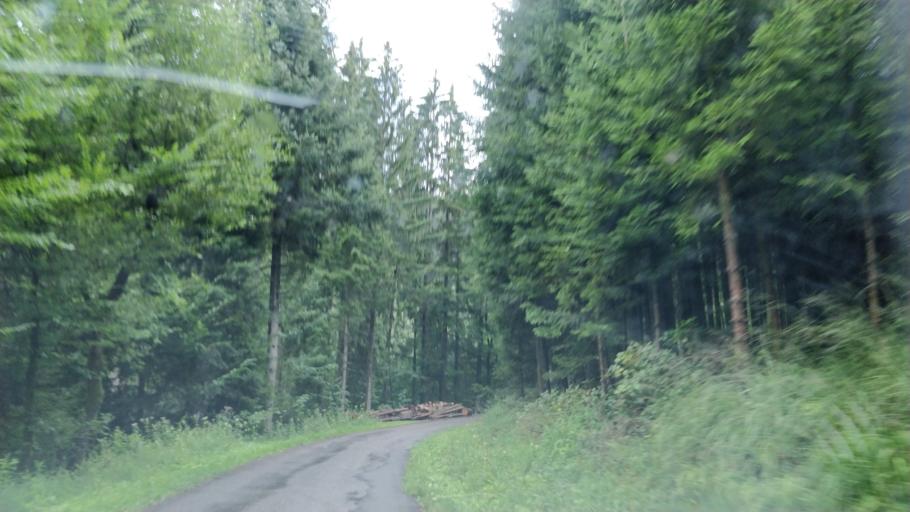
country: DE
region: Baden-Wuerttemberg
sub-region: Regierungsbezirk Stuttgart
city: Murrhardt
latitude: 49.0009
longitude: 9.5555
